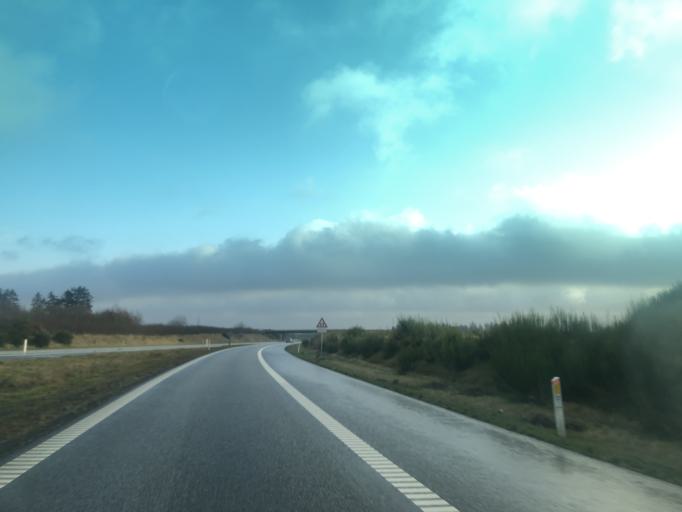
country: DK
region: Central Jutland
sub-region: Herning Kommune
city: Snejbjerg
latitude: 56.1914
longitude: 8.8964
